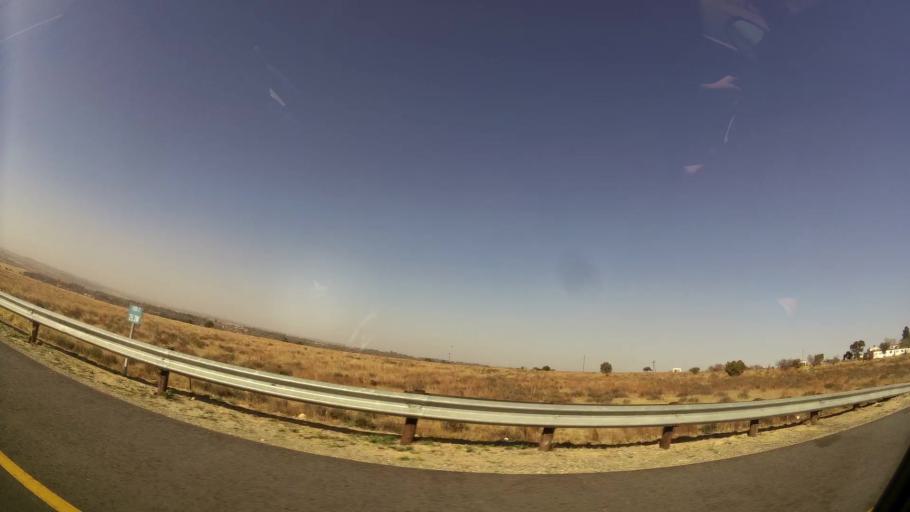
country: ZA
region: Gauteng
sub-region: City of Johannesburg Metropolitan Municipality
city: Diepsloot
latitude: -25.9671
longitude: 27.9475
